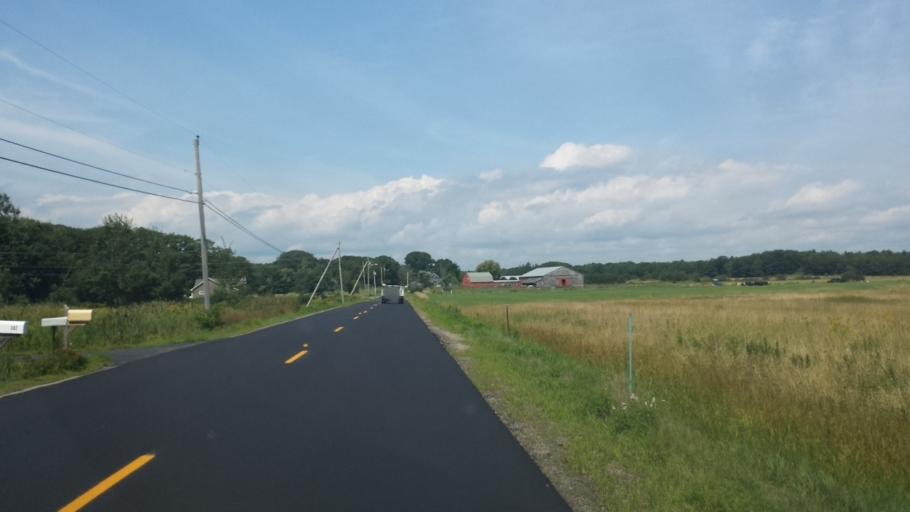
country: US
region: Maine
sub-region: York County
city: Biddeford
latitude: 43.4297
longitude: -70.4015
